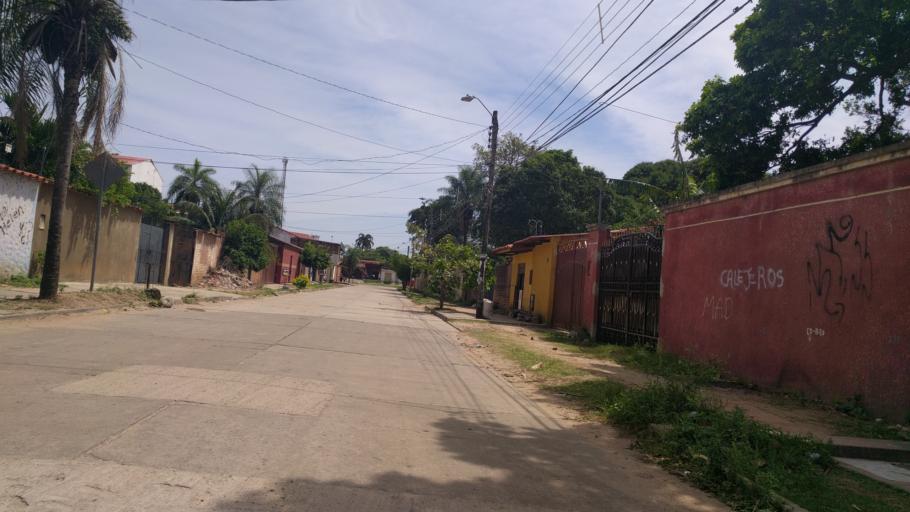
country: BO
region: Santa Cruz
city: Santa Cruz de la Sierra
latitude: -17.8152
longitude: -63.2213
